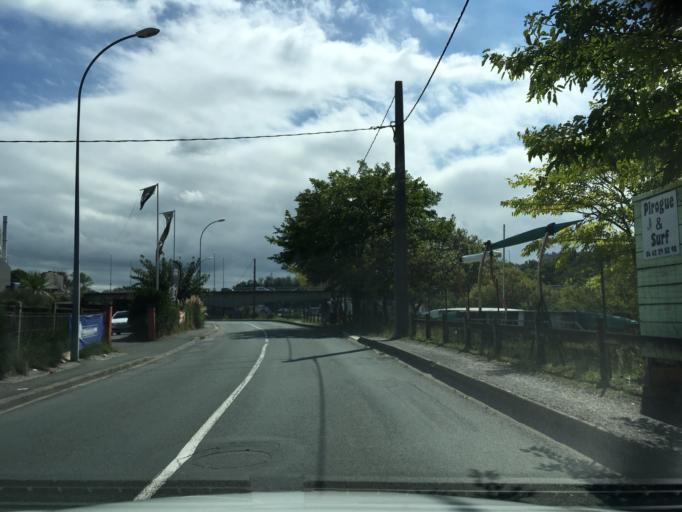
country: FR
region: Aquitaine
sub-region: Departement des Pyrenees-Atlantiques
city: Bayonne
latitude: 43.4892
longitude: -1.4623
